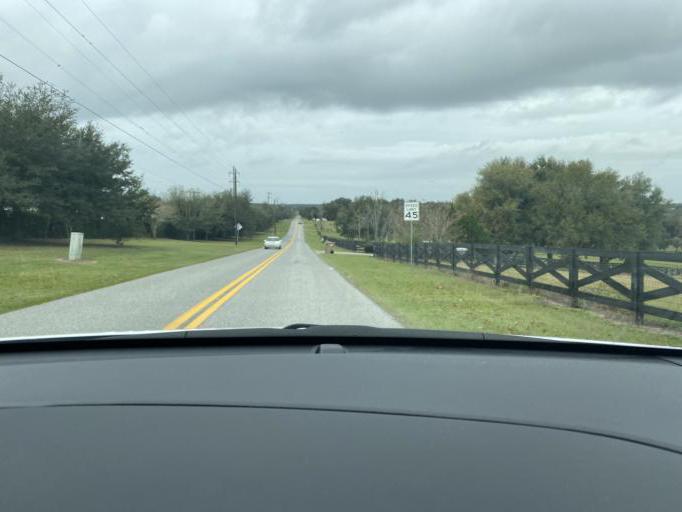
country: US
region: Florida
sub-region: Lake County
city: Minneola
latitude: 28.5948
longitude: -81.7714
